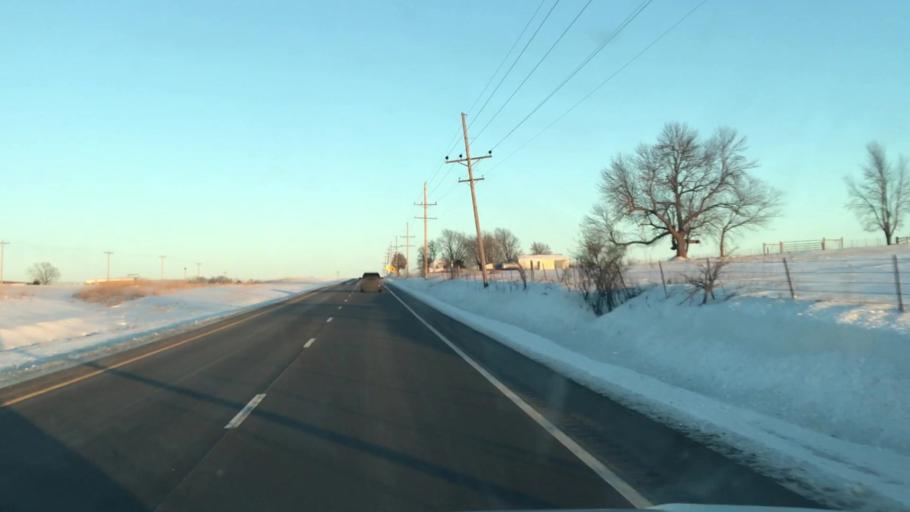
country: US
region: Missouri
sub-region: Clinton County
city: Cameron
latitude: 39.7546
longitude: -94.3057
